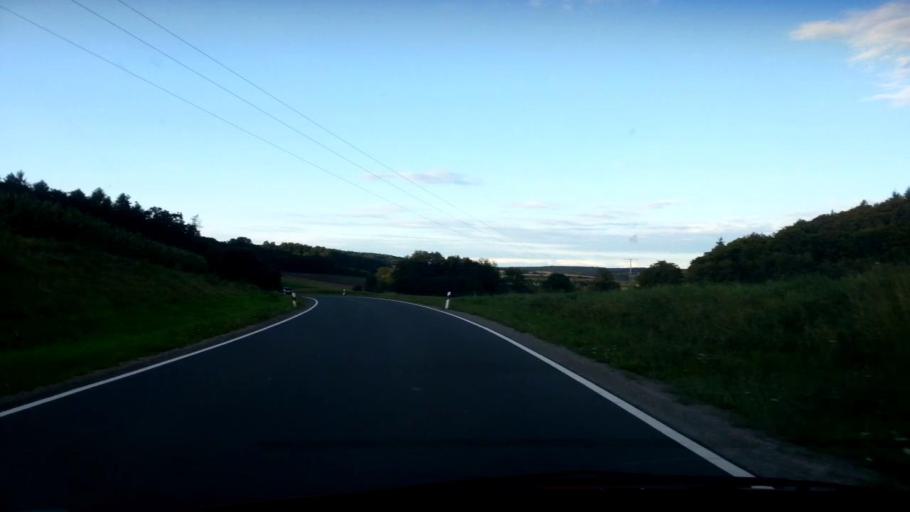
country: DE
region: Bavaria
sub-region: Upper Franconia
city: Burgwindheim
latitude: 49.8211
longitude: 10.5596
